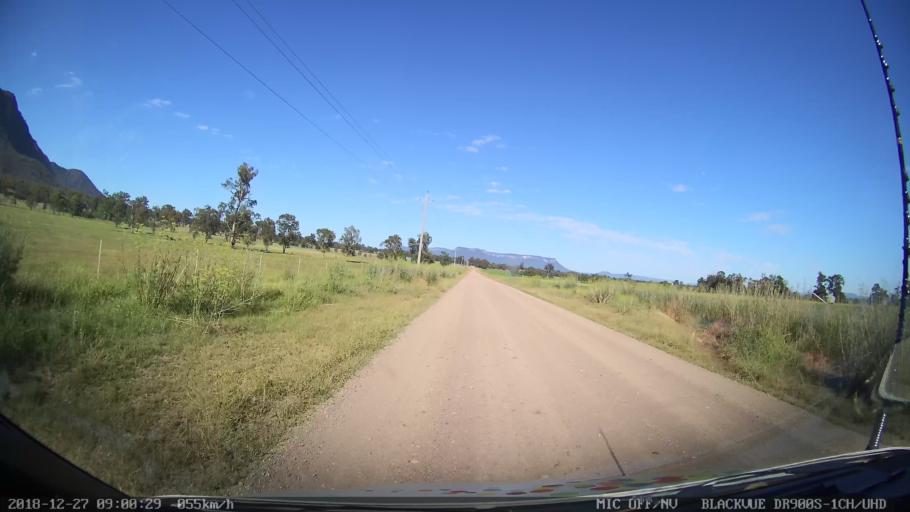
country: AU
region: New South Wales
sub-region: Lithgow
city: Portland
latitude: -33.1011
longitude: 150.2261
